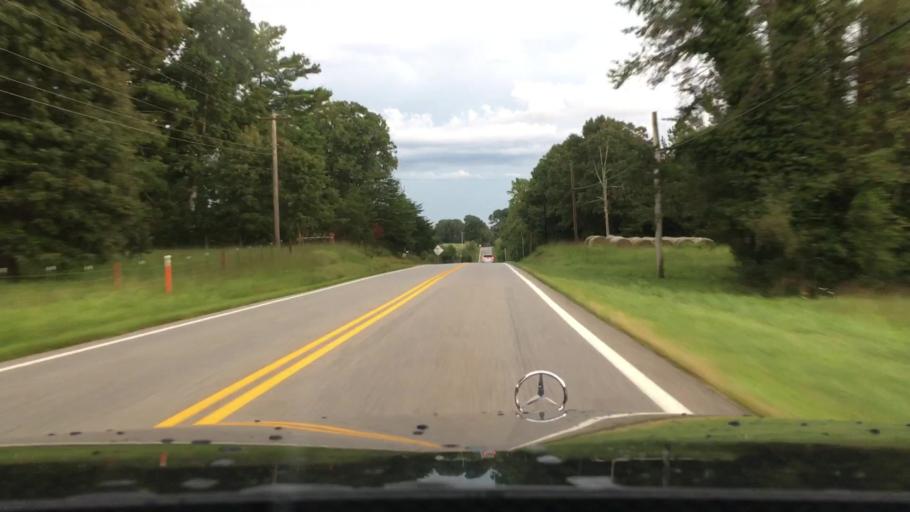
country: US
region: Virginia
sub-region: Amherst County
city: Amherst
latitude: 37.6337
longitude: -79.0207
